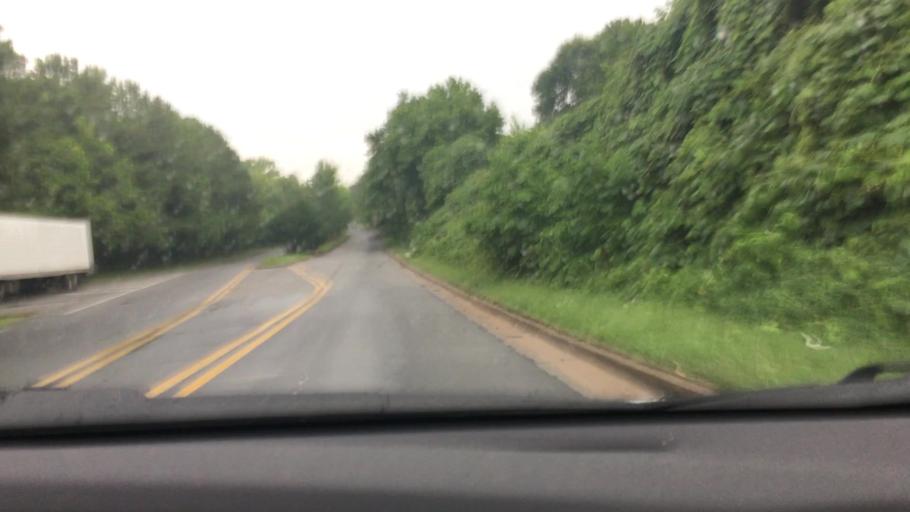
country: US
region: Georgia
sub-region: Fulton County
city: Union City
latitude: 33.6548
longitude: -84.5215
